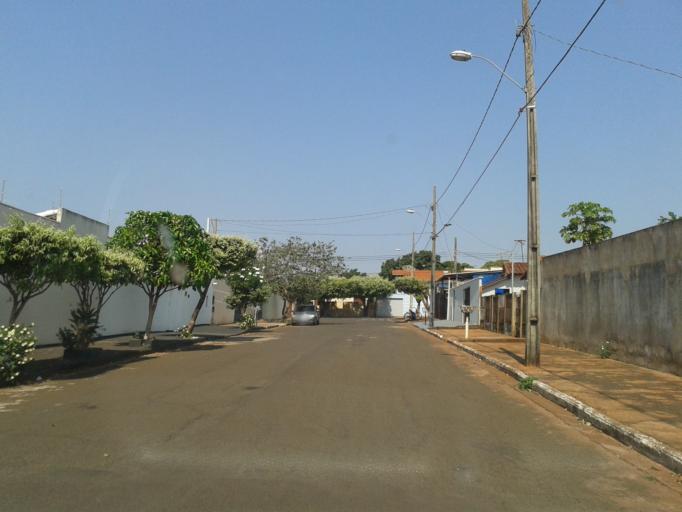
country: BR
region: Minas Gerais
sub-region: Ituiutaba
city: Ituiutaba
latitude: -18.9723
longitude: -49.4761
